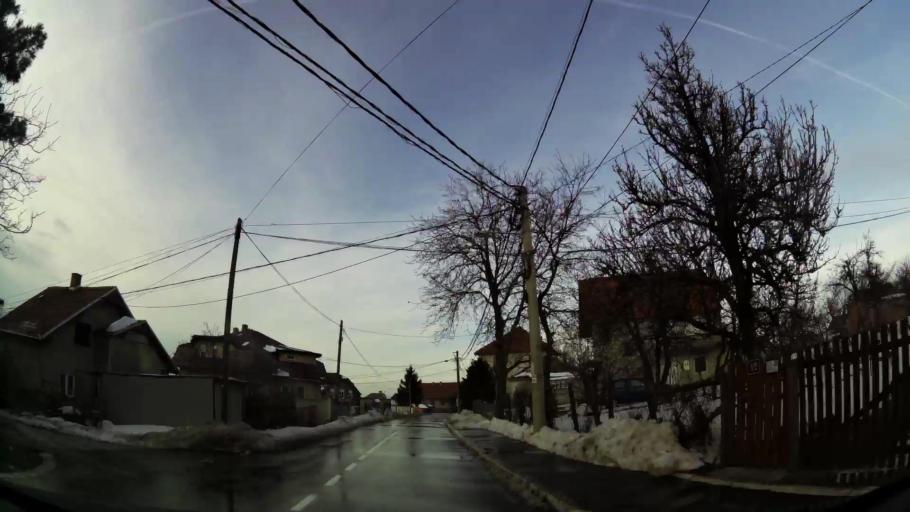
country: RS
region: Central Serbia
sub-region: Belgrade
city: Zvezdara
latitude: 44.7345
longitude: 20.5113
